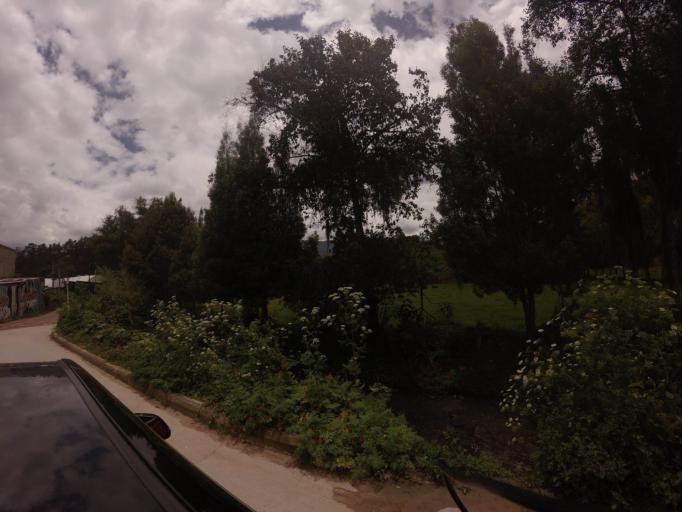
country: CO
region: Boyaca
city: Duitama
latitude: 5.8263
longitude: -73.0231
